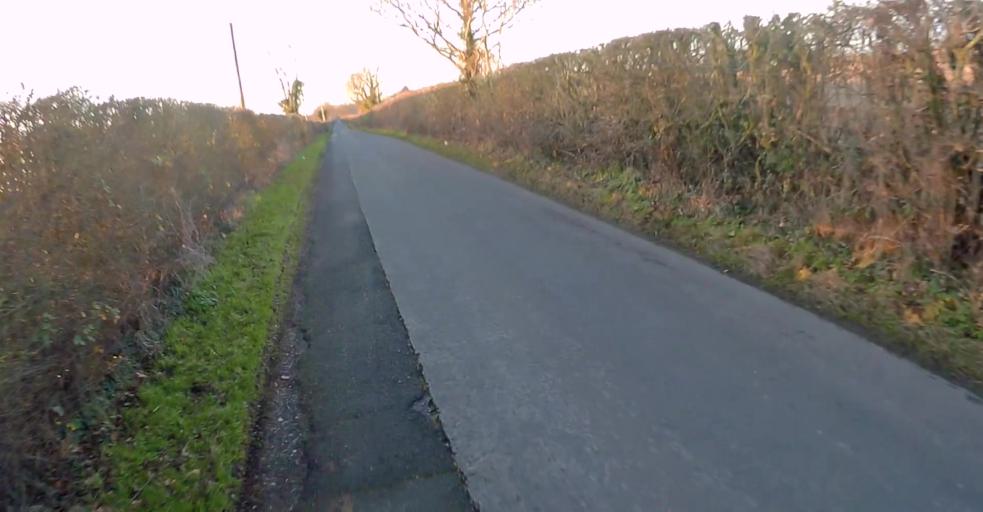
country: GB
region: England
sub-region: West Berkshire
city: Stratfield Mortimer
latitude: 51.3481
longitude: -1.0142
